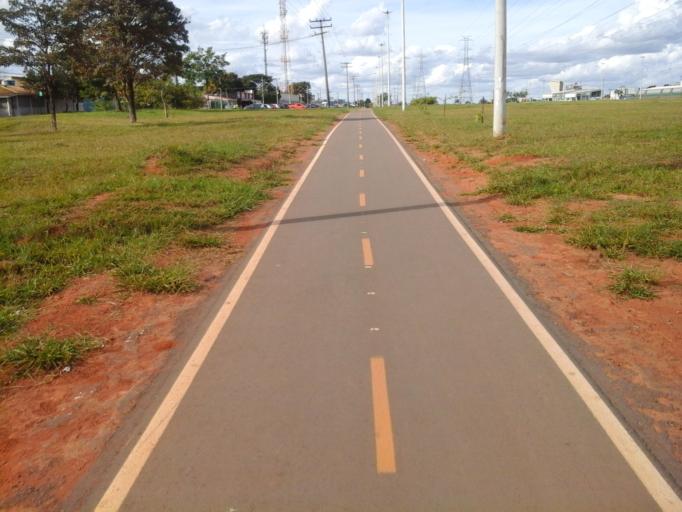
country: BR
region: Federal District
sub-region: Brasilia
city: Brasilia
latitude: -15.8267
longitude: -47.9860
